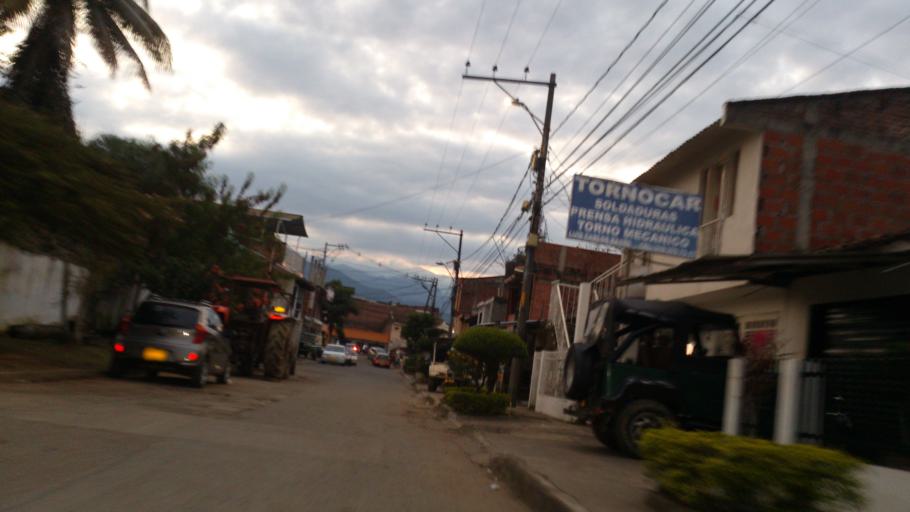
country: CO
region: Valle del Cauca
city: Jamundi
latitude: 3.2634
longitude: -76.5371
